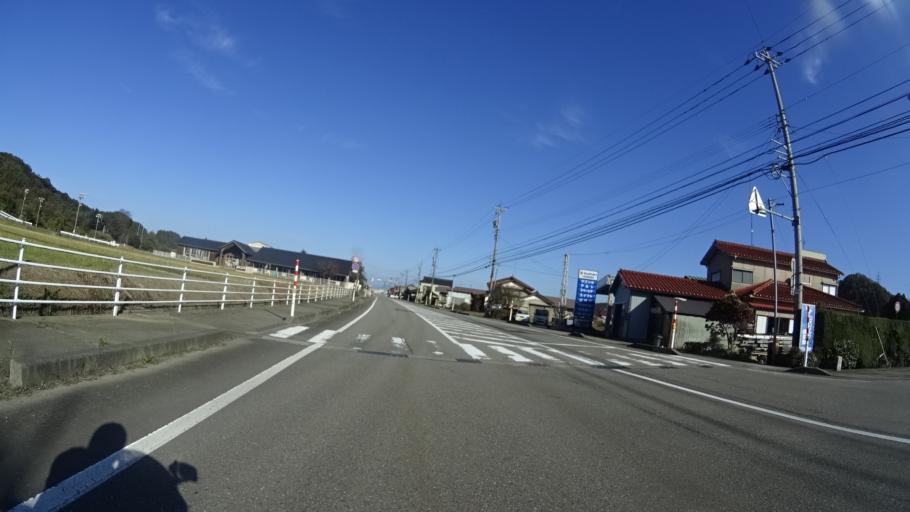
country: JP
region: Ishikawa
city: Komatsu
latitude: 36.2831
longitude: 136.3911
